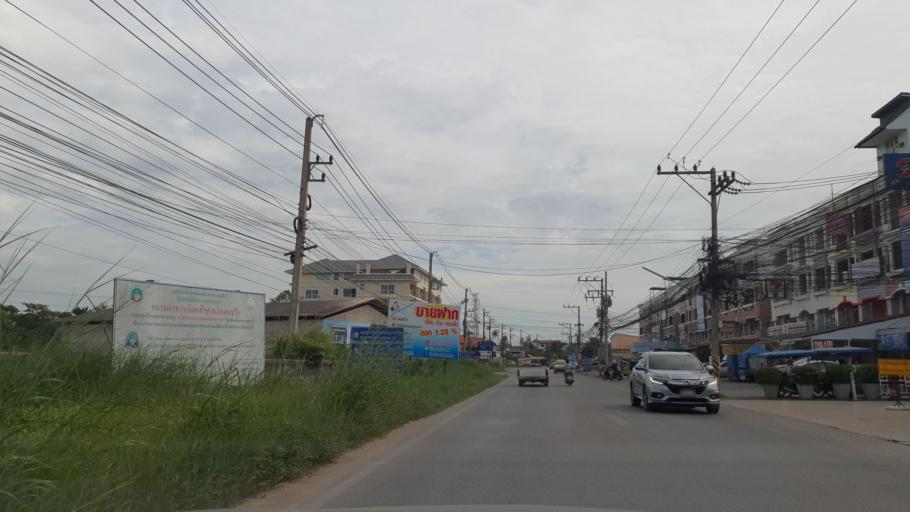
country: TH
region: Chon Buri
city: Phatthaya
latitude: 12.9577
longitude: 100.9257
